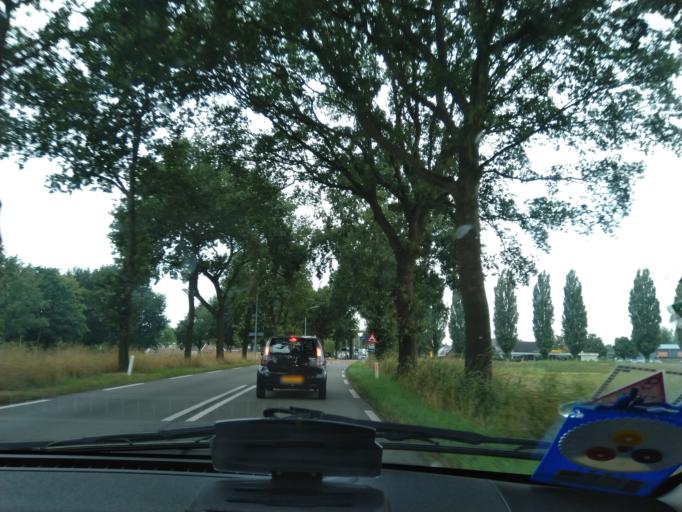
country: NL
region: Groningen
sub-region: Gemeente Pekela
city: Oude Pekela
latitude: 53.1117
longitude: 7.0278
